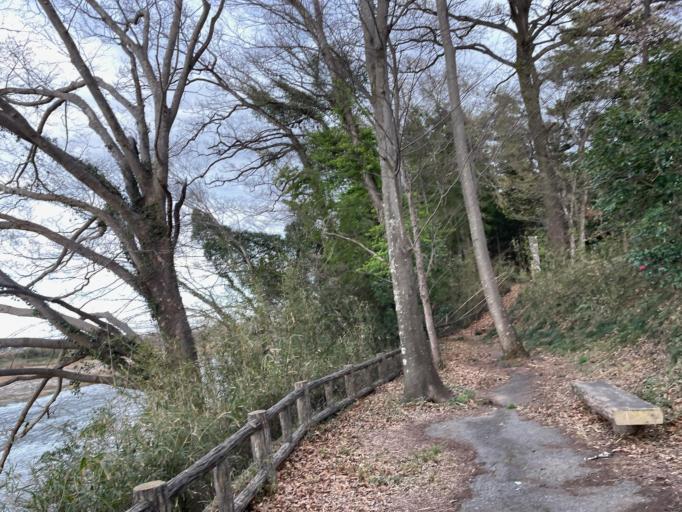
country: JP
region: Saitama
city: Fukayacho
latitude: 36.1331
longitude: 139.2696
